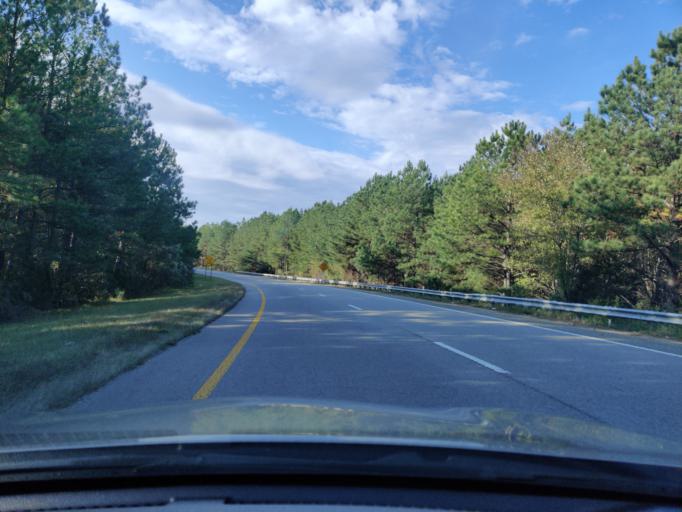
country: US
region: North Carolina
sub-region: Wake County
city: Morrisville
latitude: 35.8937
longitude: -78.8151
